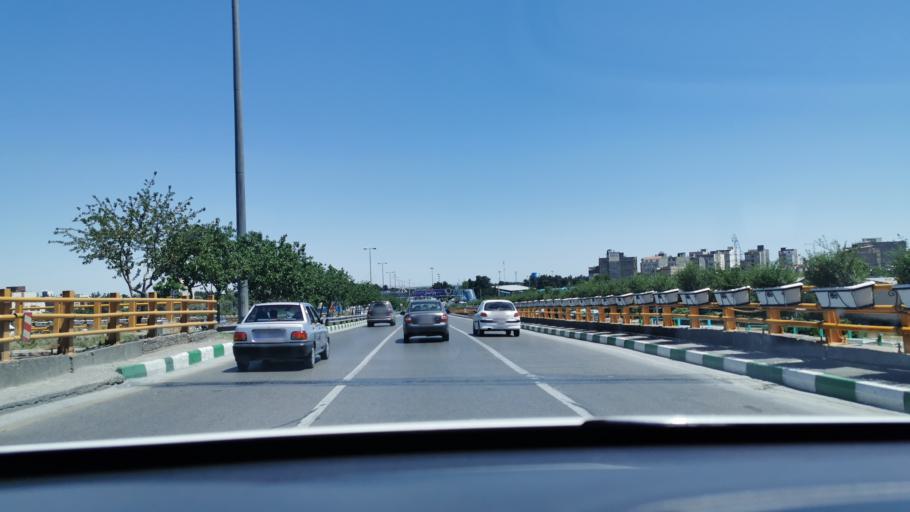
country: IR
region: Razavi Khorasan
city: Mashhad
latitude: 36.2555
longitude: 59.5994
